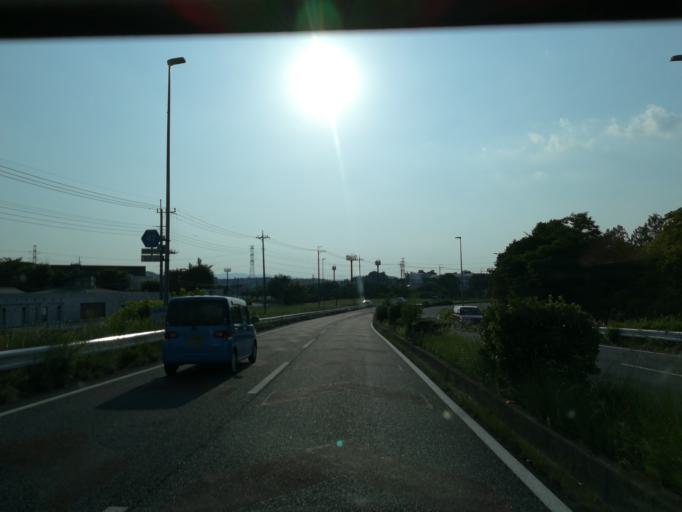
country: JP
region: Saitama
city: Kumagaya
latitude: 36.0668
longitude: 139.3647
